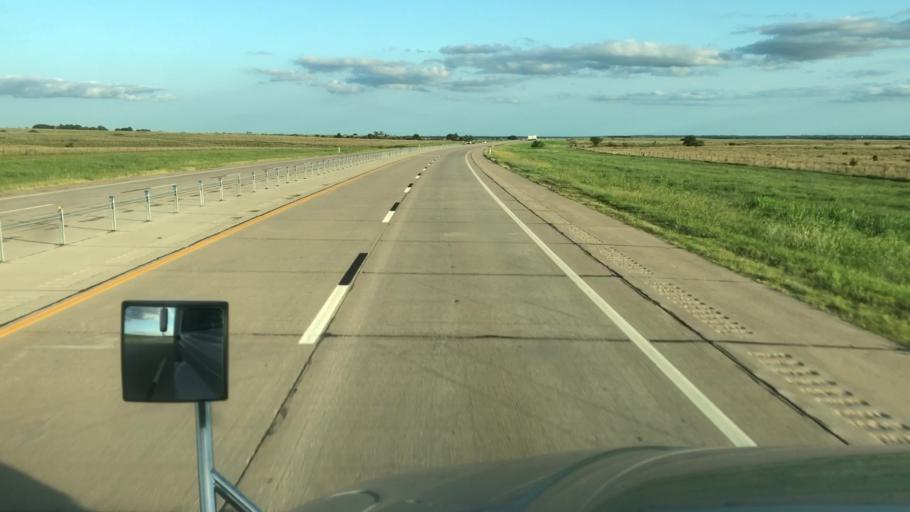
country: US
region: Oklahoma
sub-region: Pawnee County
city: Pawnee
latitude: 36.3688
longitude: -97.0363
